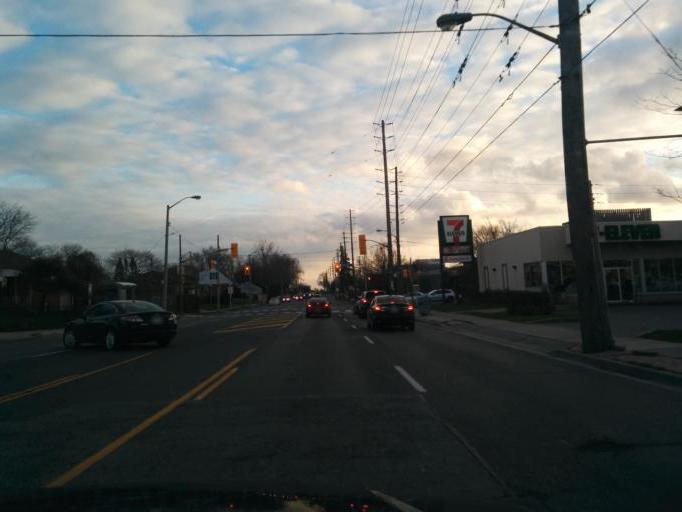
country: CA
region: Ontario
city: Etobicoke
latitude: 43.6296
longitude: -79.5173
